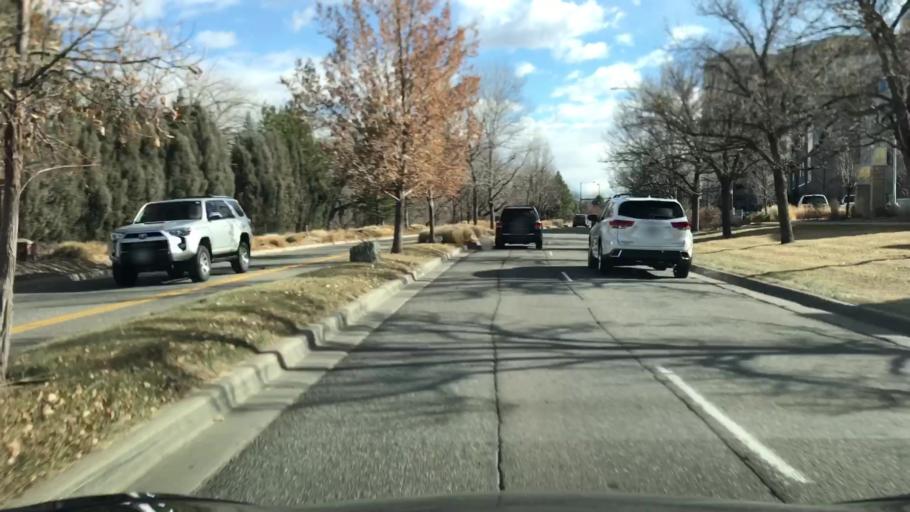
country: US
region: Colorado
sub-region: Arapahoe County
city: Glendale
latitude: 39.7058
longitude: -104.9391
